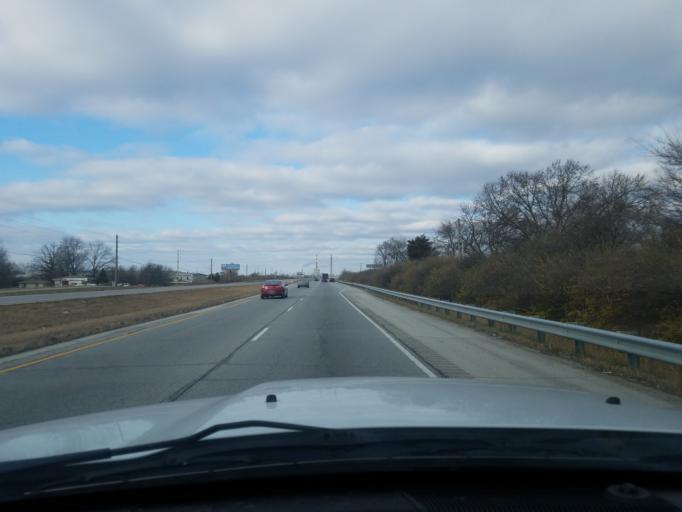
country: US
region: Indiana
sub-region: Marion County
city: Southport
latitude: 39.6761
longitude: -86.1959
